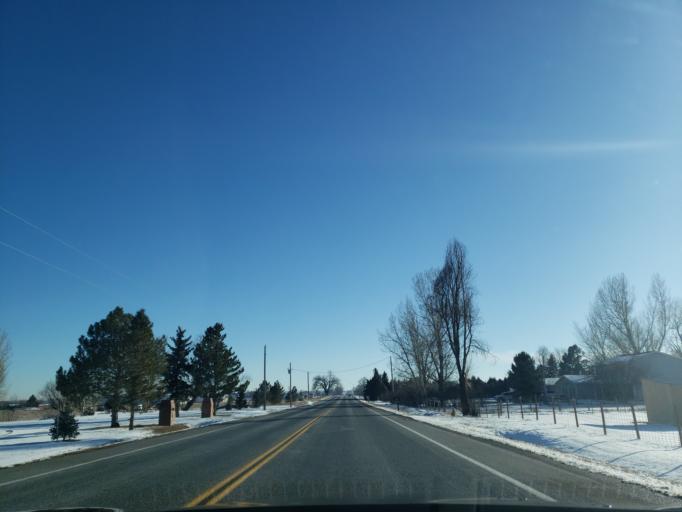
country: US
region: Colorado
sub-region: Weld County
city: Windsor
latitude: 40.5119
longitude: -105.0009
